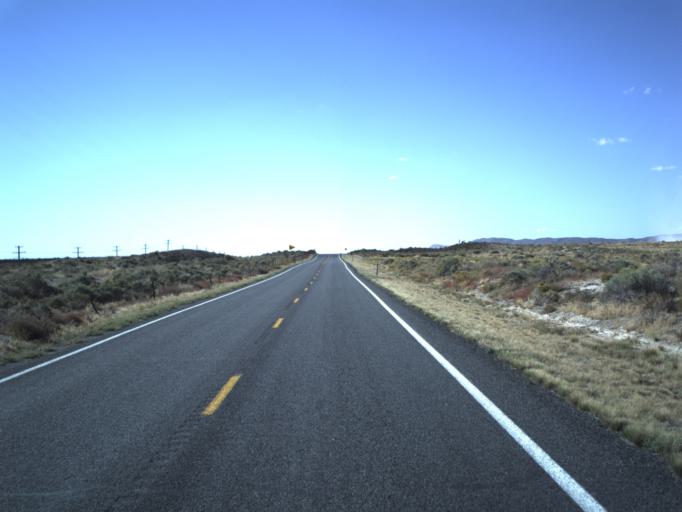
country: US
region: Utah
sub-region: Millard County
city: Delta
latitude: 38.9614
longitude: -112.8029
